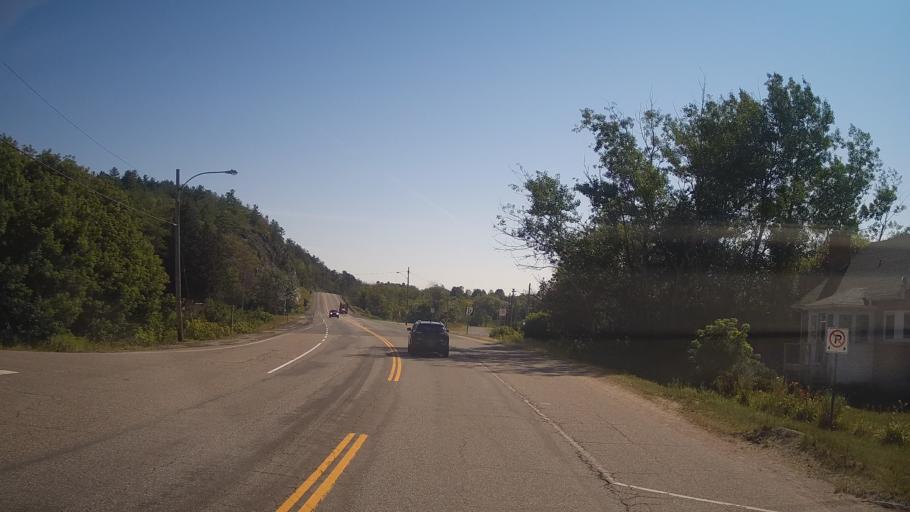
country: CA
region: Ontario
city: Espanola
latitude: 46.2700
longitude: -81.8850
